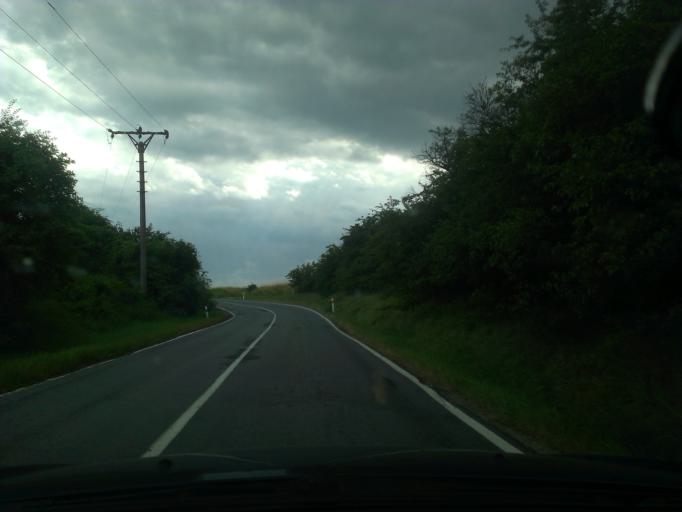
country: CZ
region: South Moravian
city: Velka nad Velickou
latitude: 48.8595
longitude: 17.5225
